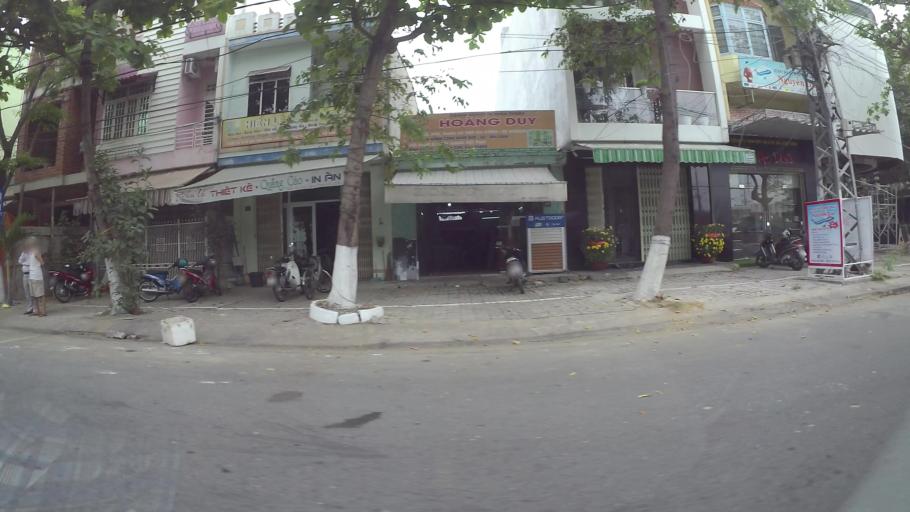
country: VN
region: Da Nang
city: Cam Le
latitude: 16.0367
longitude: 108.2142
